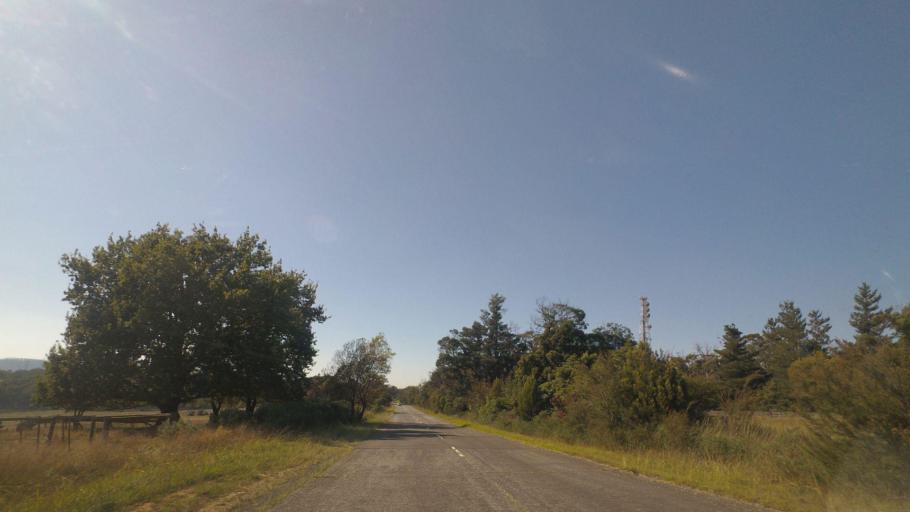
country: AU
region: Victoria
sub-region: Cardinia
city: Garfield
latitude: -38.0716
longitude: 145.6501
